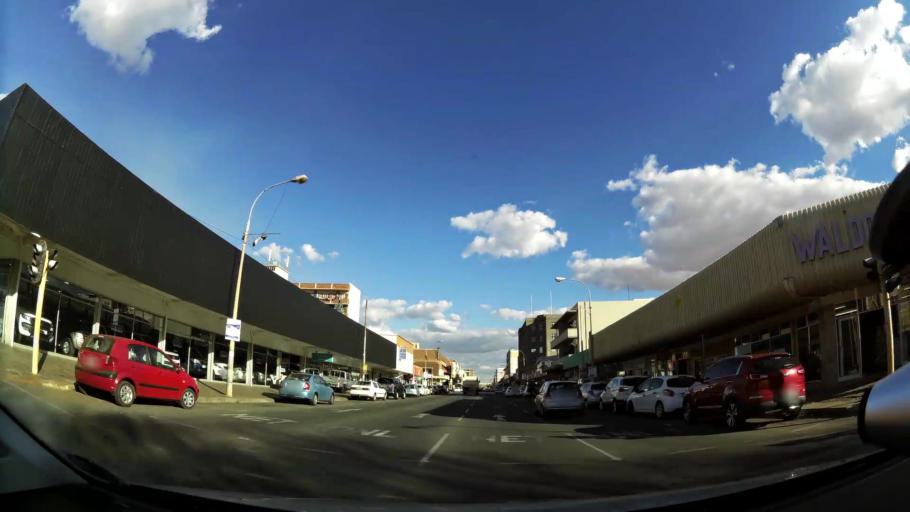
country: ZA
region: North-West
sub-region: Dr Kenneth Kaunda District Municipality
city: Klerksdorp
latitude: -26.8667
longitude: 26.6661
